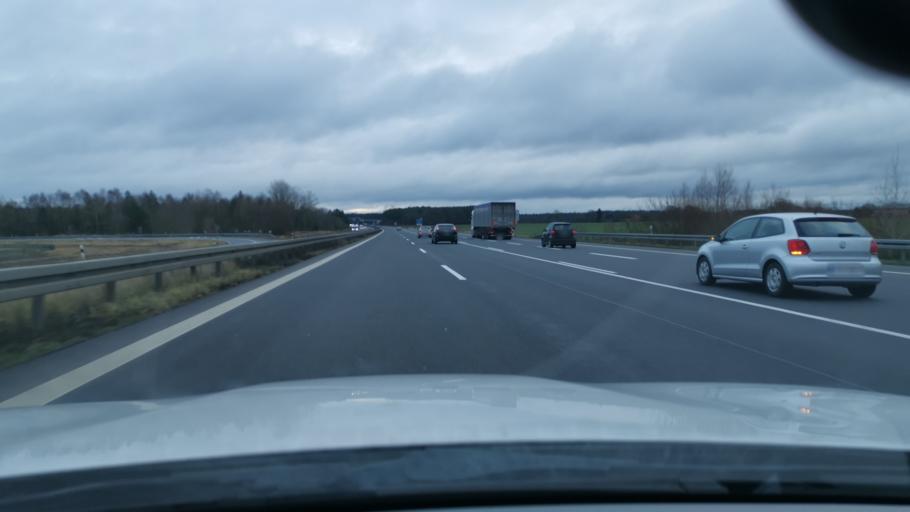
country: DE
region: Brandenburg
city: Wittstock
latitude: 53.1297
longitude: 12.4598
